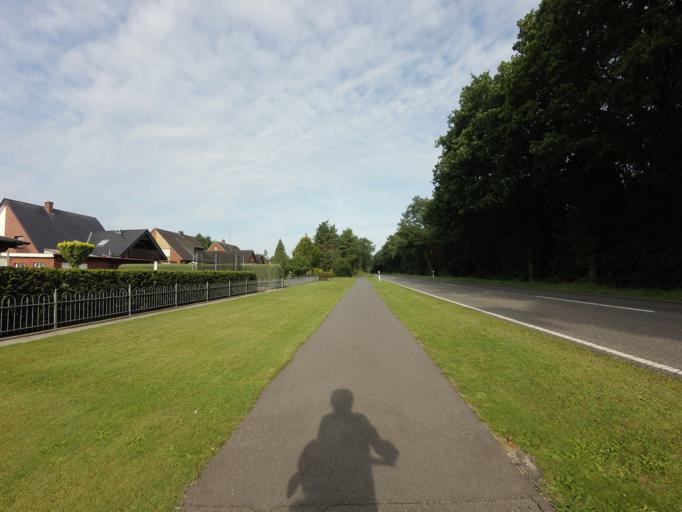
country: DE
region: Lower Saxony
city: Itterbeck
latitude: 52.5074
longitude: 6.7936
